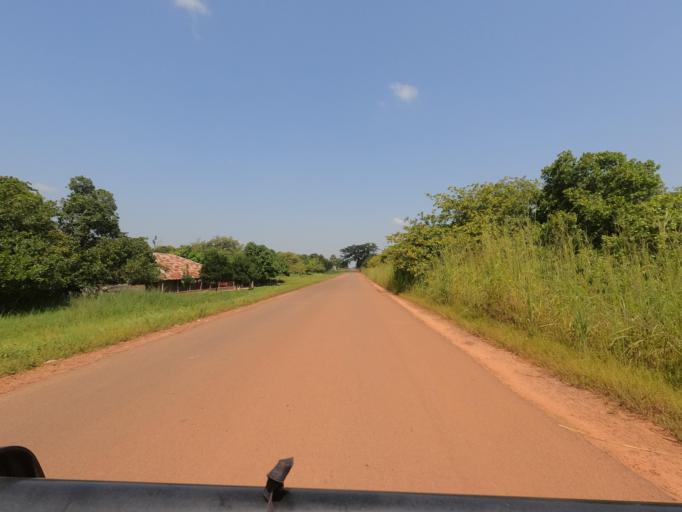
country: SN
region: Ziguinchor
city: Adeane
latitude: 12.3686
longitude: -15.7757
